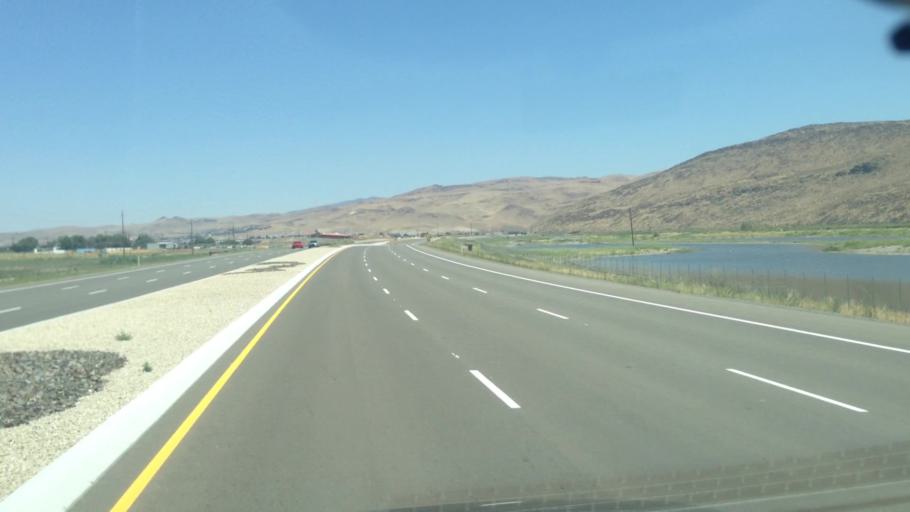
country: US
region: Nevada
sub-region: Washoe County
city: Sparks
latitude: 39.5007
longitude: -119.7268
